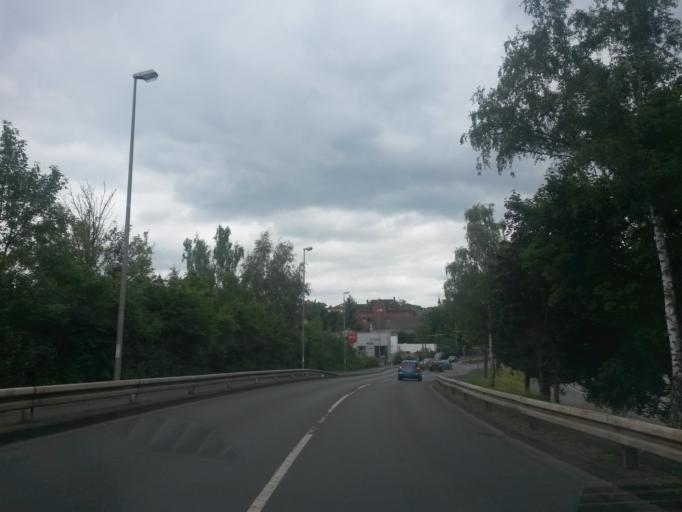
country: DE
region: Hesse
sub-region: Regierungsbezirk Kassel
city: Bad Hersfeld
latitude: 50.8631
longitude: 9.7058
